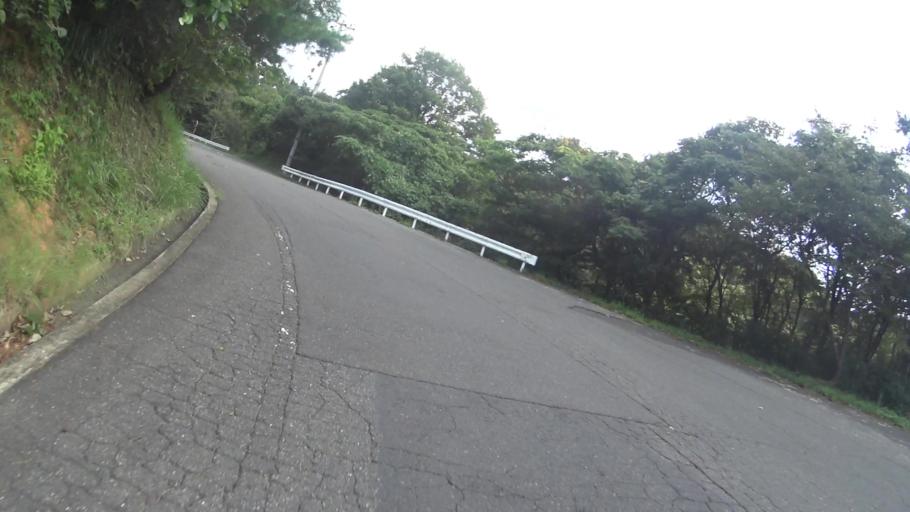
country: JP
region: Kyoto
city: Miyazu
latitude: 35.7324
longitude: 135.1769
